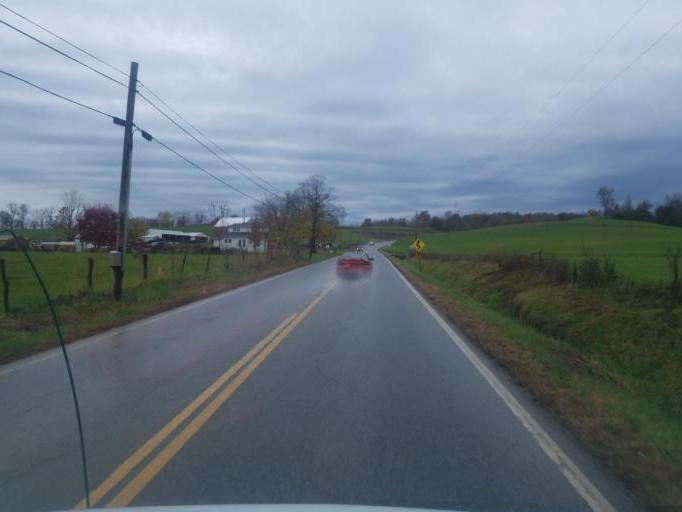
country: US
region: Ohio
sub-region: Morgan County
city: McConnelsville
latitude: 39.5047
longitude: -81.8561
